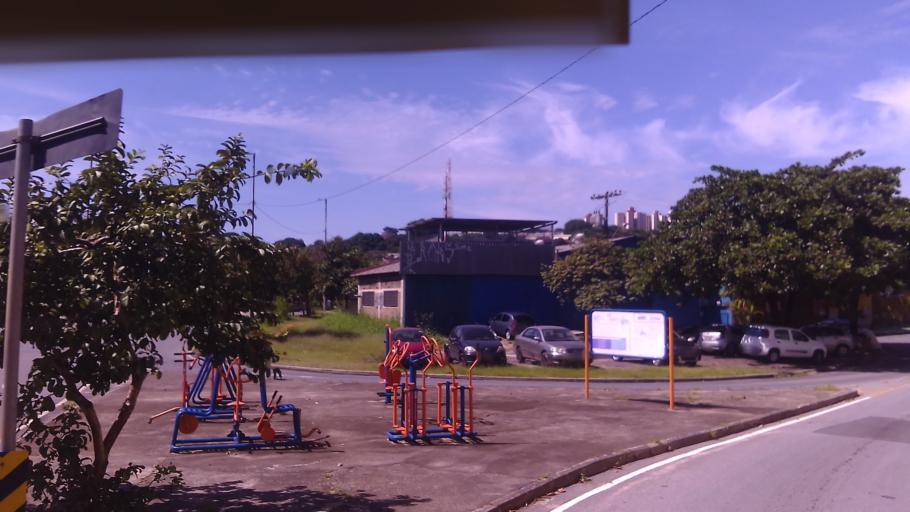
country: BR
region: Minas Gerais
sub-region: Belo Horizonte
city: Belo Horizonte
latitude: -19.9290
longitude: -43.9942
